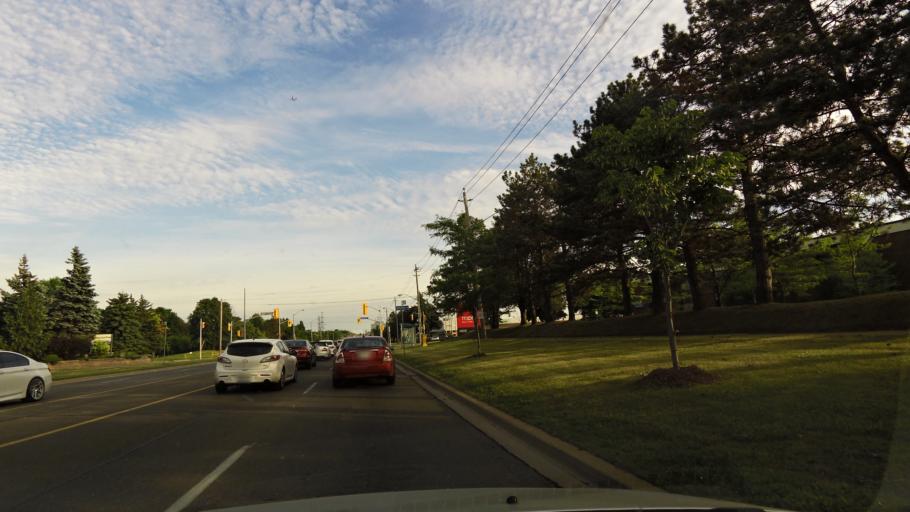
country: CA
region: Ontario
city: Concord
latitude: 43.7787
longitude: -79.4693
